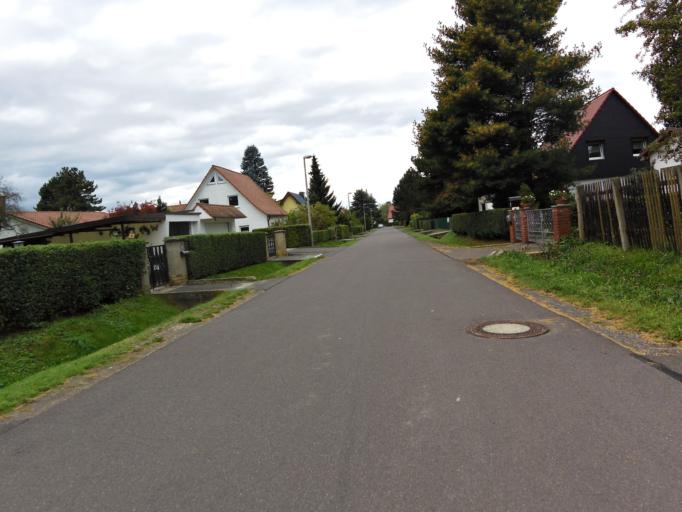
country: DE
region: Saxony
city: Grossposna
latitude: 51.2896
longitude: 12.4392
